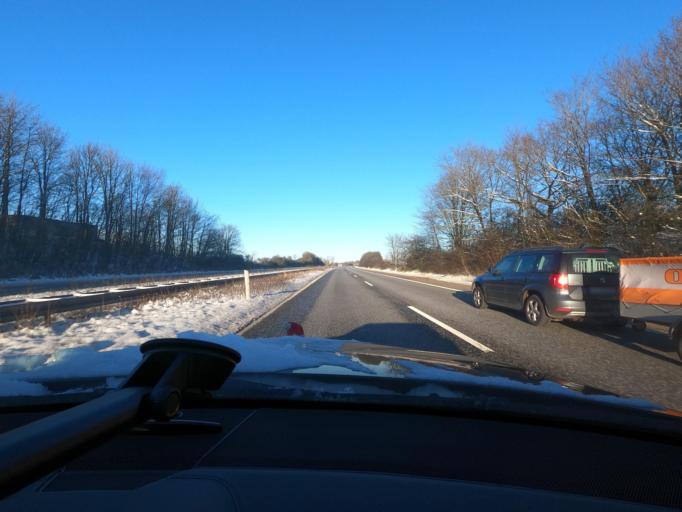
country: DK
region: South Denmark
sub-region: Aabenraa Kommune
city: Rodekro
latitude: 55.0436
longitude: 9.3527
